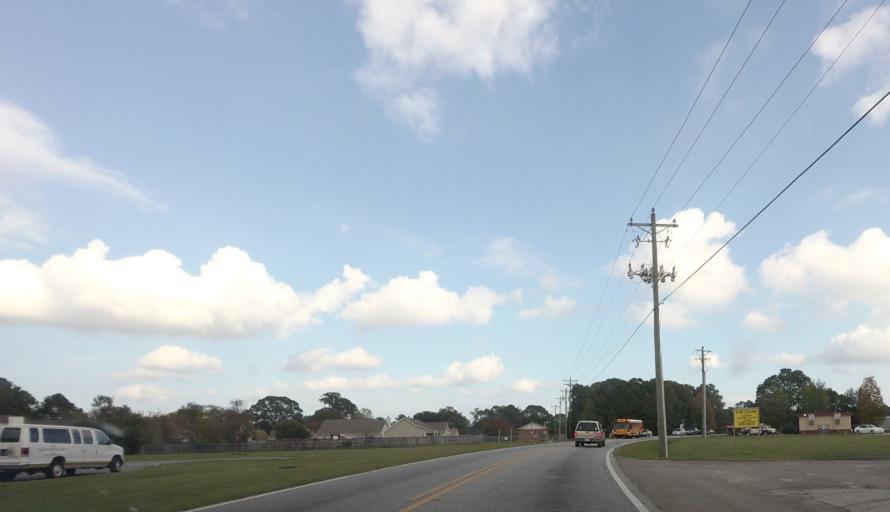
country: US
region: Georgia
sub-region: Houston County
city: Centerville
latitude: 32.6345
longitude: -83.6554
